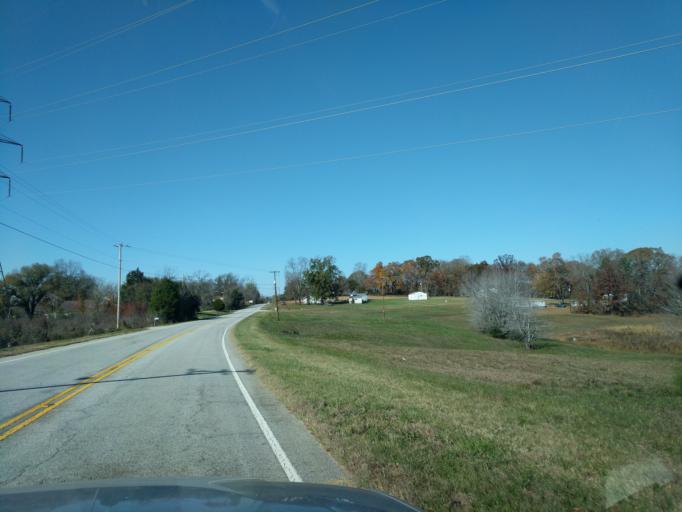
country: US
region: South Carolina
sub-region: Greenville County
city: Tigerville
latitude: 34.9990
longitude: -82.3536
